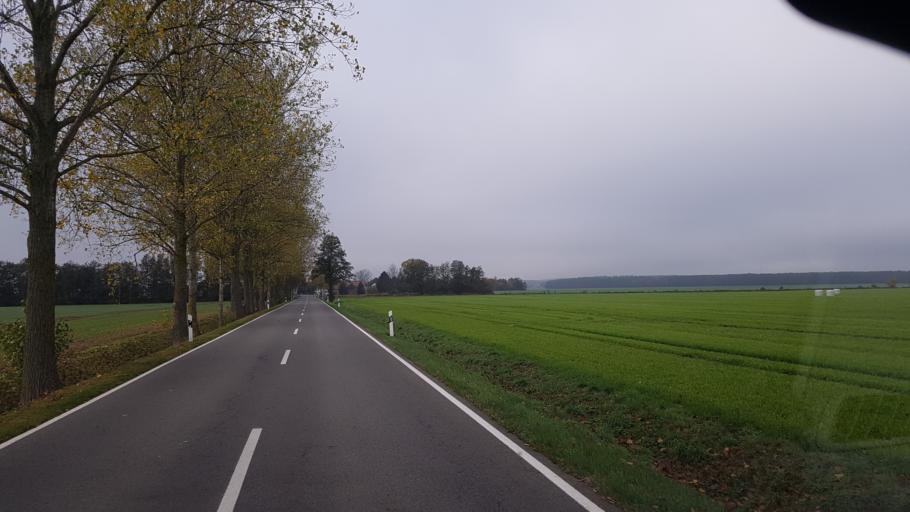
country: DE
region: Brandenburg
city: Schonewalde
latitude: 51.6924
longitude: 13.5467
